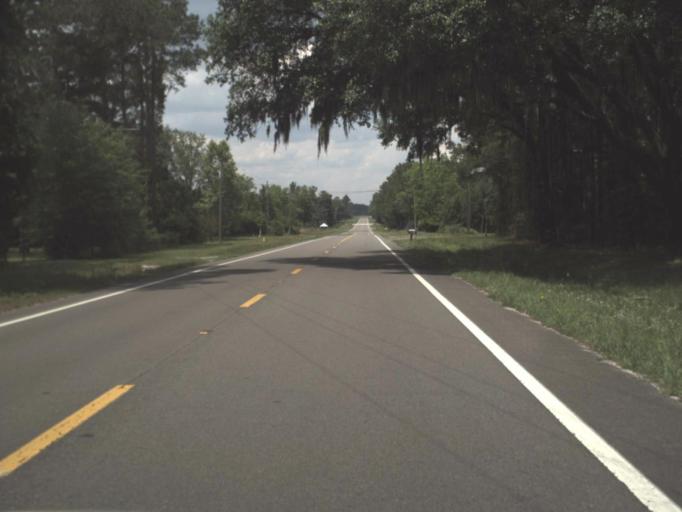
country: US
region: Florida
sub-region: Columbia County
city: Five Points
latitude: 30.2906
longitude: -82.6306
